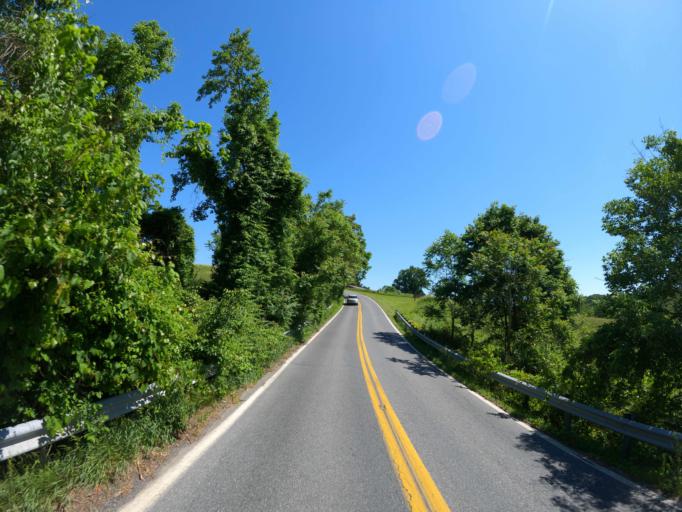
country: US
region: Maryland
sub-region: Frederick County
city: Green Valley
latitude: 39.2798
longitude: -77.2746
